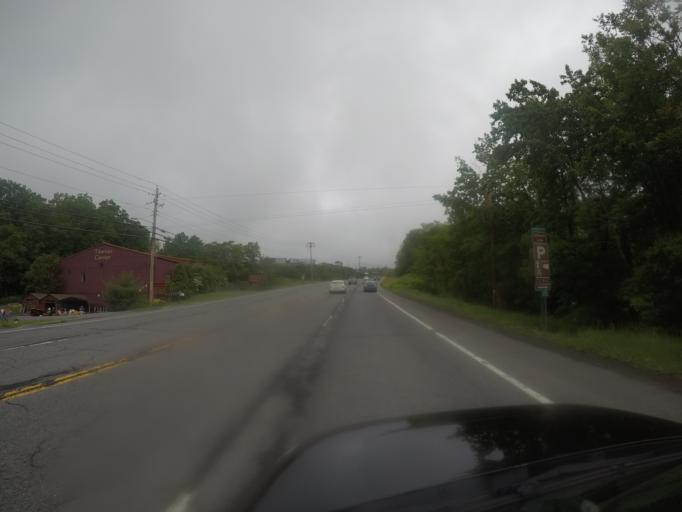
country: US
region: New York
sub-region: Ulster County
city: West Hurley
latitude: 41.9786
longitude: -74.0851
